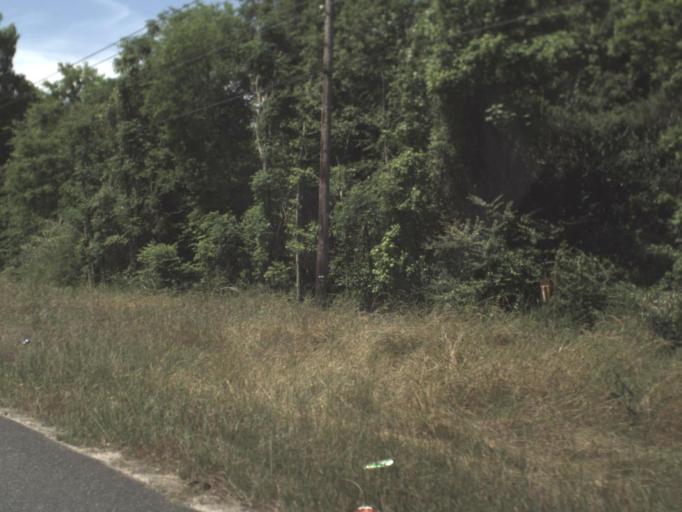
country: US
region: Florida
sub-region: Jackson County
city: Marianna
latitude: 30.8022
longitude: -85.2136
